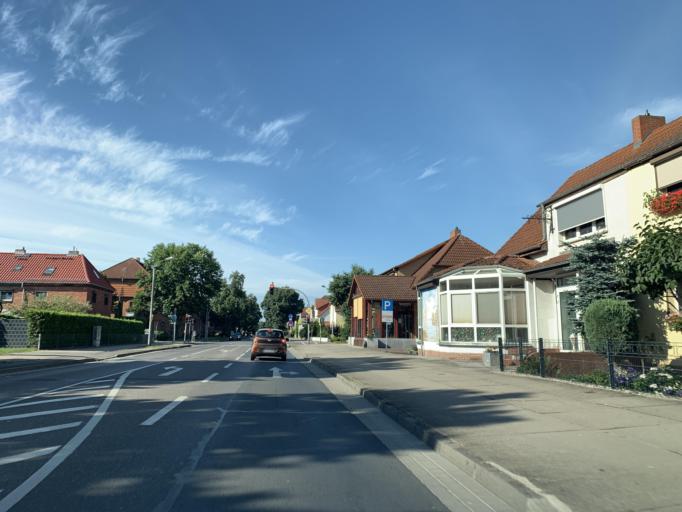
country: DE
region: Mecklenburg-Vorpommern
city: Neubrandenburg
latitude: 53.5678
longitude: 13.2750
